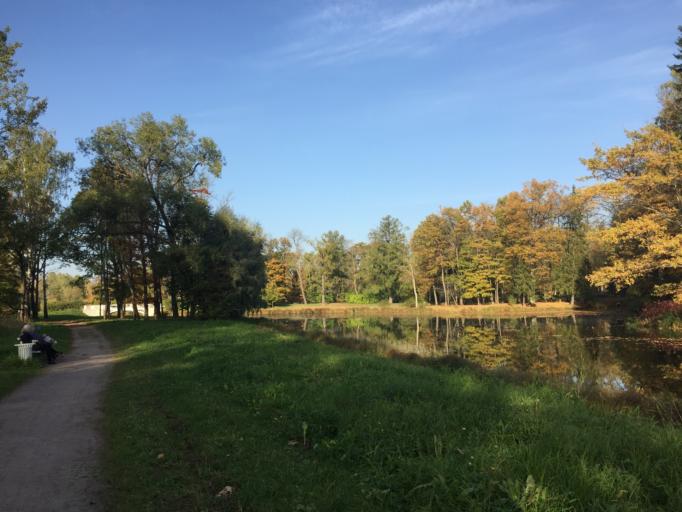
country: RU
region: St.-Petersburg
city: Pushkin
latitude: 59.7208
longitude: 30.3717
